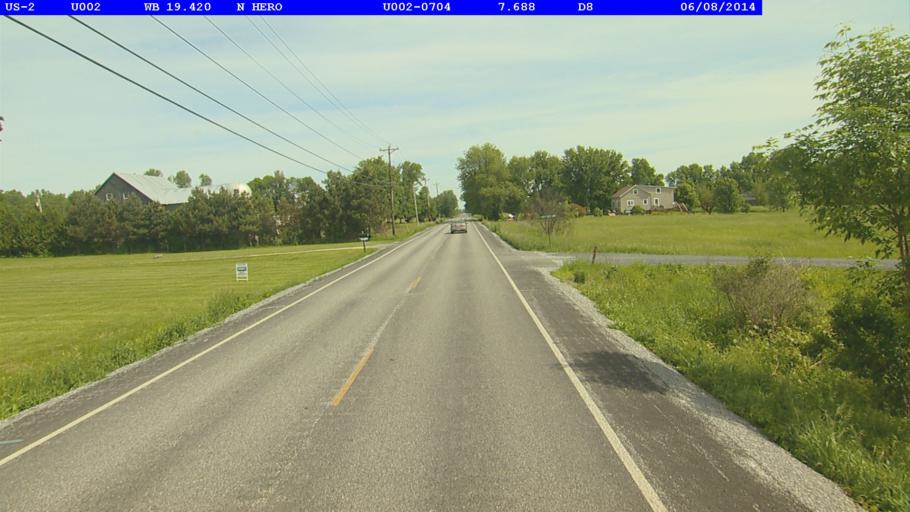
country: US
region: Vermont
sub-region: Grand Isle County
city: North Hero
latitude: 44.7889
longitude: -73.2929
